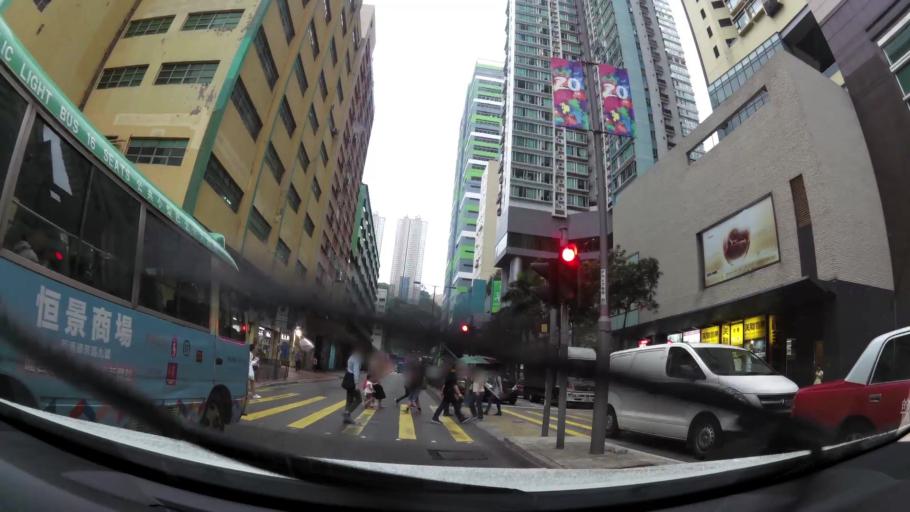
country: HK
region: Tsuen Wan
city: Tsuen Wan
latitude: 22.3670
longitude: 114.1178
